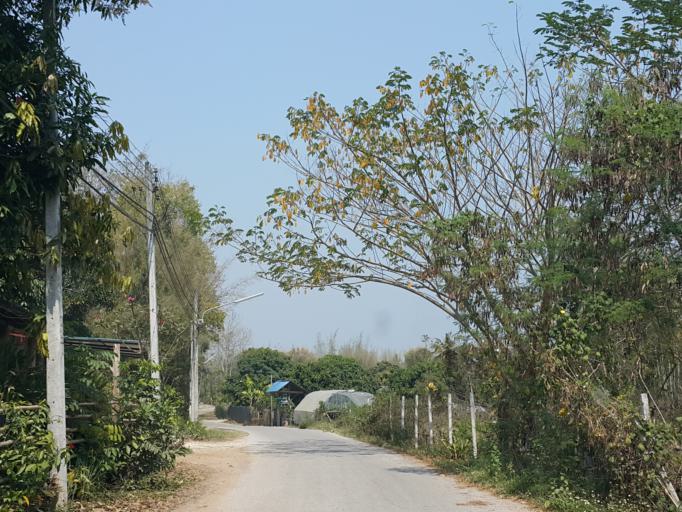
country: TH
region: Chiang Mai
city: San Sai
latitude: 18.9476
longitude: 98.9185
